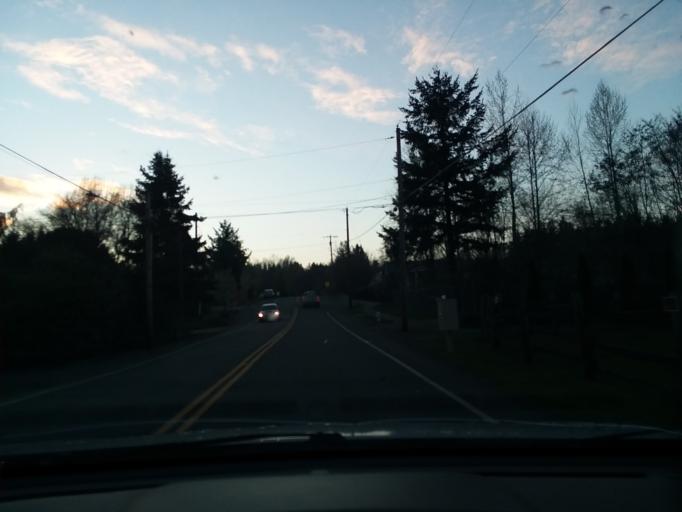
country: US
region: Washington
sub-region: King County
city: Kenmore
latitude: 47.7776
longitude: -122.2507
